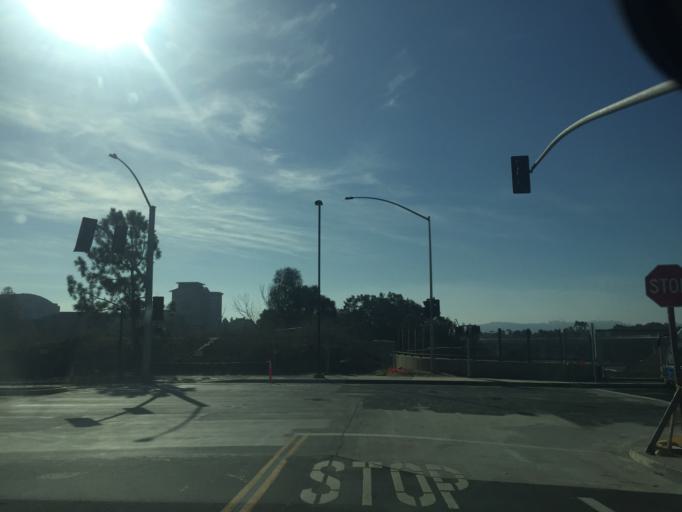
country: US
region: California
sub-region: San Diego County
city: La Jolla
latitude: 32.8761
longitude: -117.2280
